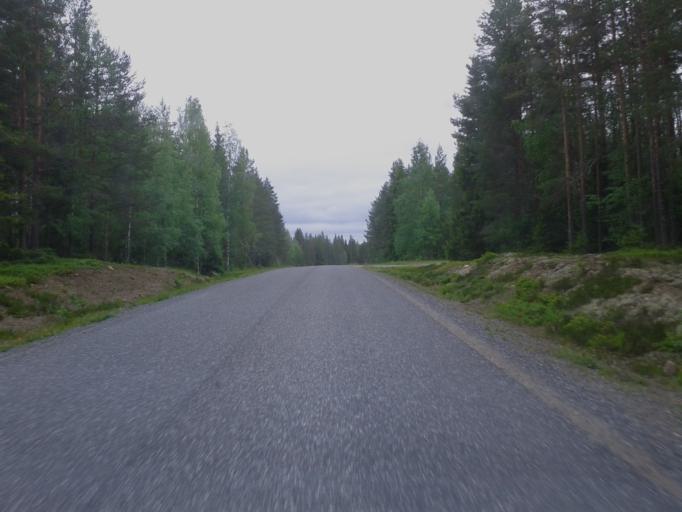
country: SE
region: Vaesterbotten
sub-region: Skelleftea Kommun
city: Storvik
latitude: 64.9927
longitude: 20.7159
